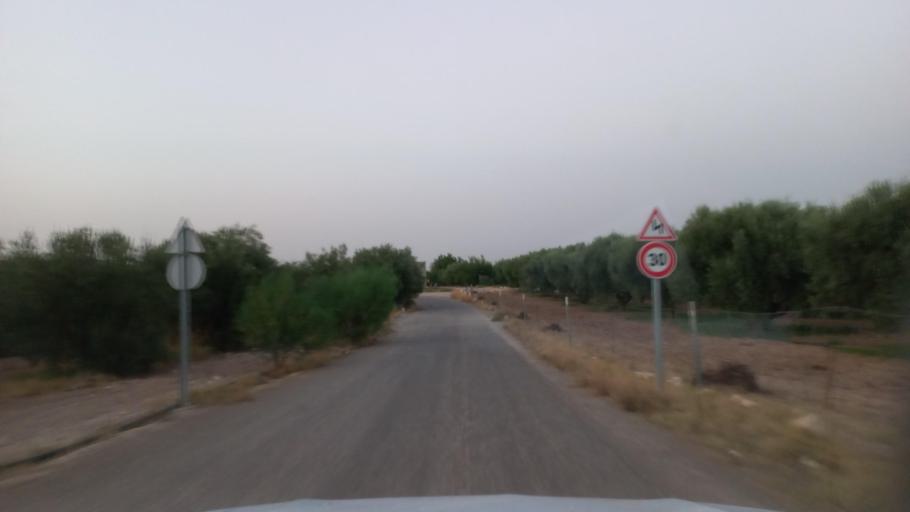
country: TN
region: Al Qasrayn
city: Kasserine
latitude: 35.2722
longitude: 9.0303
